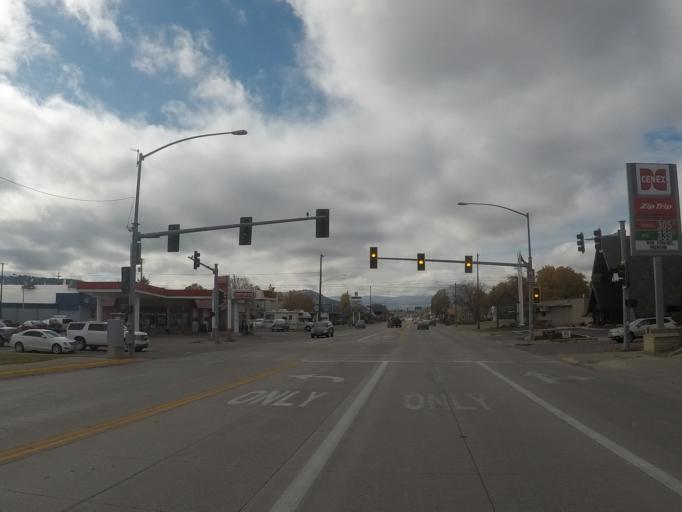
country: US
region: Montana
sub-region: Flathead County
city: Kalispell
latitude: 48.2030
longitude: -114.3094
